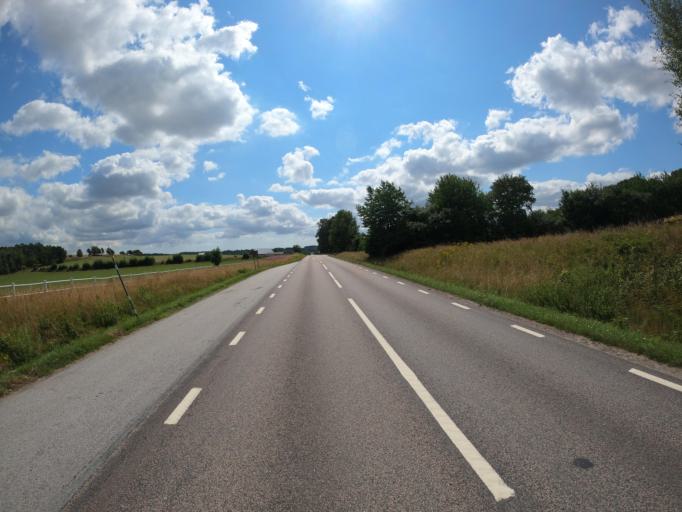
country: SE
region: Skane
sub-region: Lunds Kommun
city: Veberod
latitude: 55.6042
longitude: 13.4886
